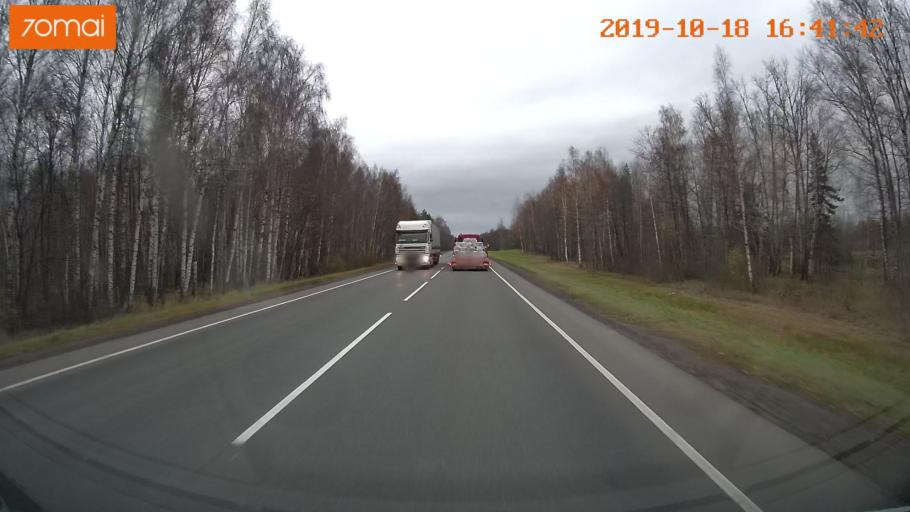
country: RU
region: Vladimir
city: Suzdal'
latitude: 56.4714
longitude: 40.4820
